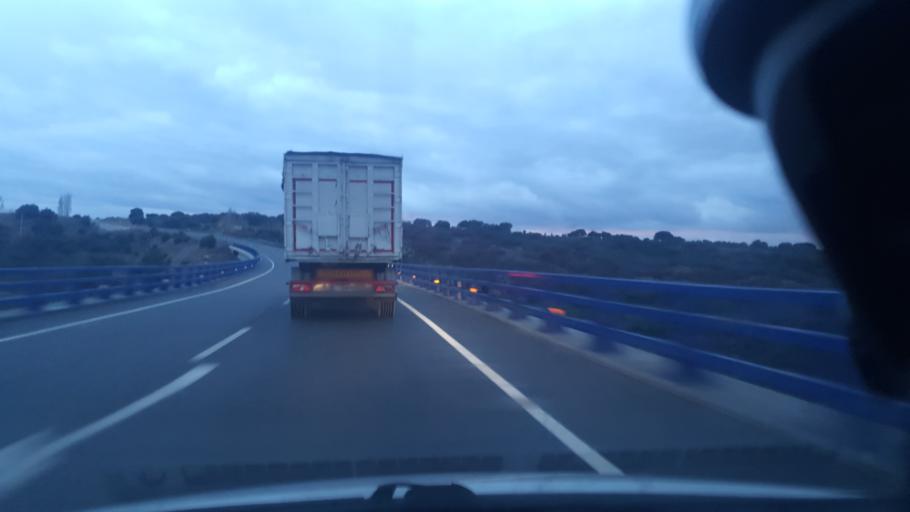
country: ES
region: Castille and Leon
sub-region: Provincia de Avila
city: Ojos-Albos
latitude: 40.7190
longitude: -4.5410
